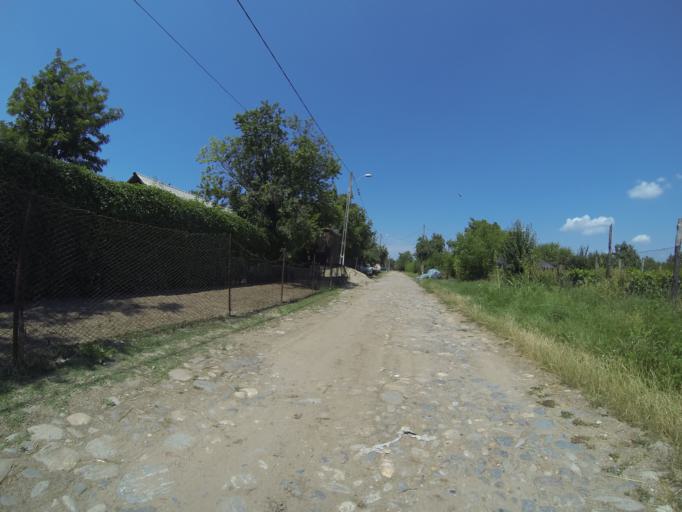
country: RO
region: Dolj
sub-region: Comuna Segarcea
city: Segarcea
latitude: 44.0864
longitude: 23.7402
